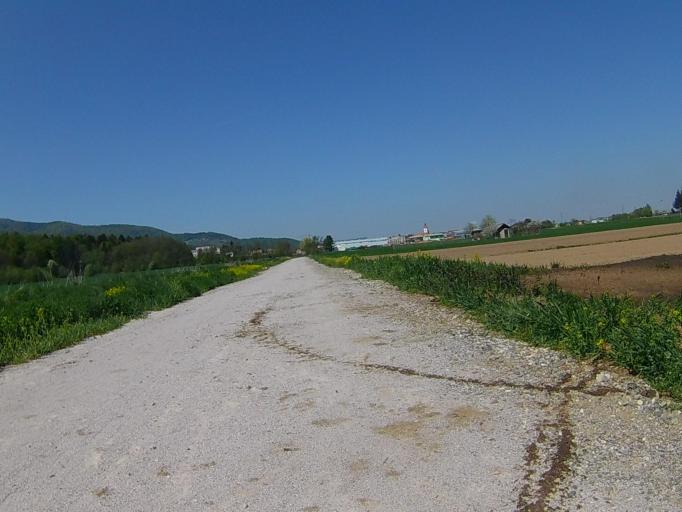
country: SI
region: Hoce-Slivnica
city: Spodnje Hoce
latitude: 46.4913
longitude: 15.6503
